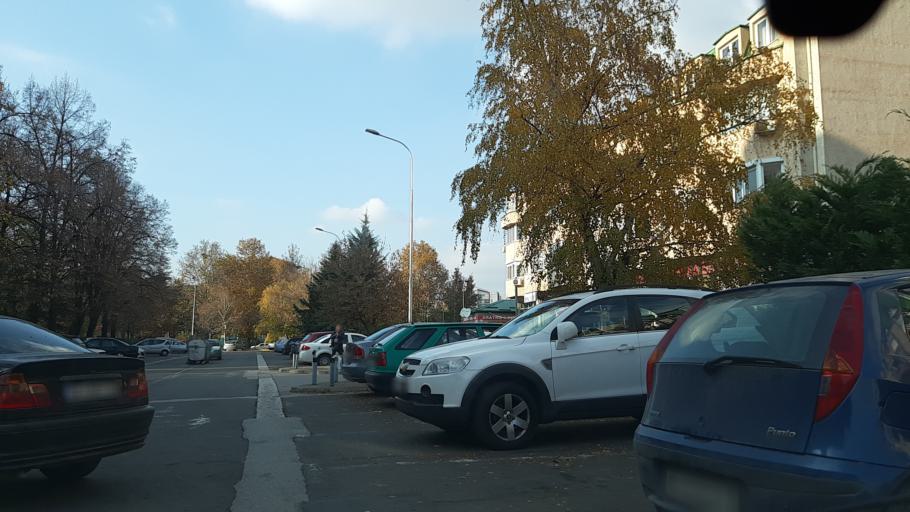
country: MK
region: Kisela Voda
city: Usje
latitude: 41.9865
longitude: 21.4629
